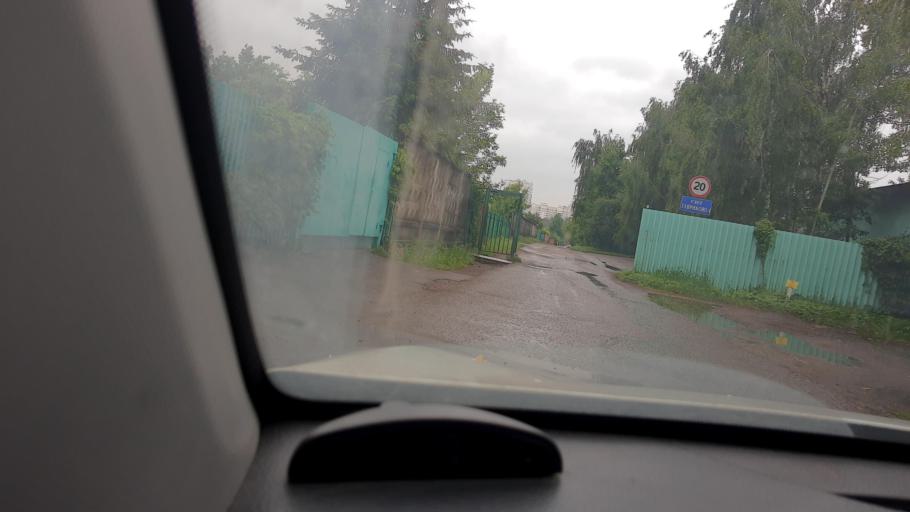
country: RU
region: Moskovskaya
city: Kommunarka
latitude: 55.5475
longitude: 37.5062
